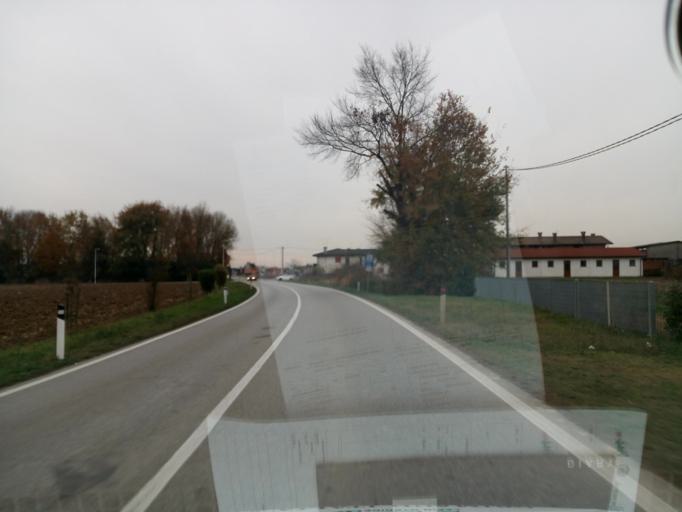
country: IT
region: Veneto
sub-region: Provincia di Padova
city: Massanzago-Ca' Baglioni-San Dono
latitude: 45.5666
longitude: 12.0032
